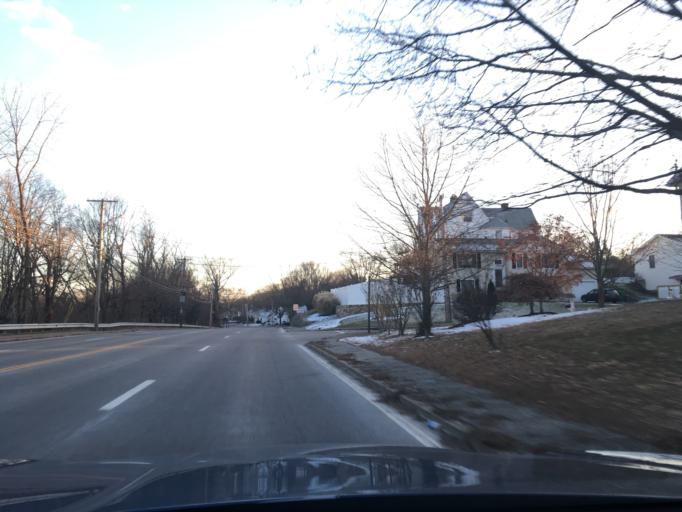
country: US
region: Rhode Island
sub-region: Kent County
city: East Greenwich
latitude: 41.7067
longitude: -71.4633
